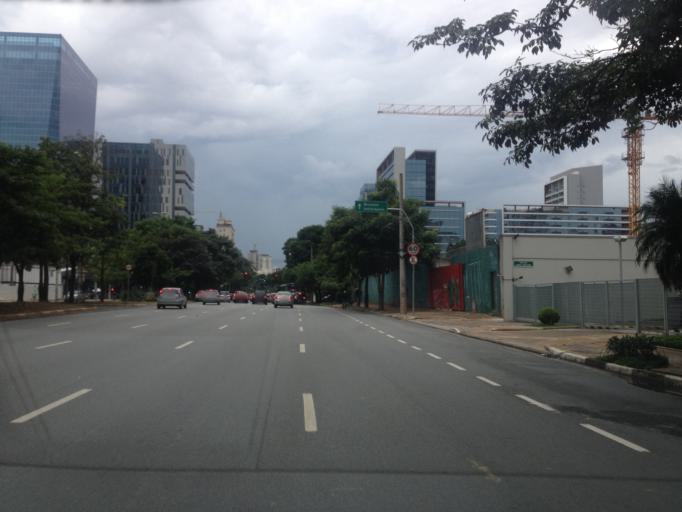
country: BR
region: Sao Paulo
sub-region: Sao Paulo
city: Sao Paulo
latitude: -23.5913
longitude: -46.6813
